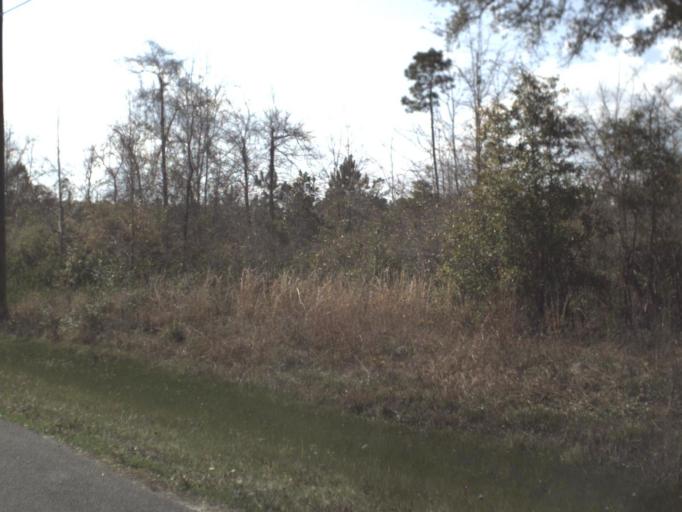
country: US
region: Florida
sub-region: Wakulla County
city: Crawfordville
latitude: 30.0671
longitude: -84.4620
